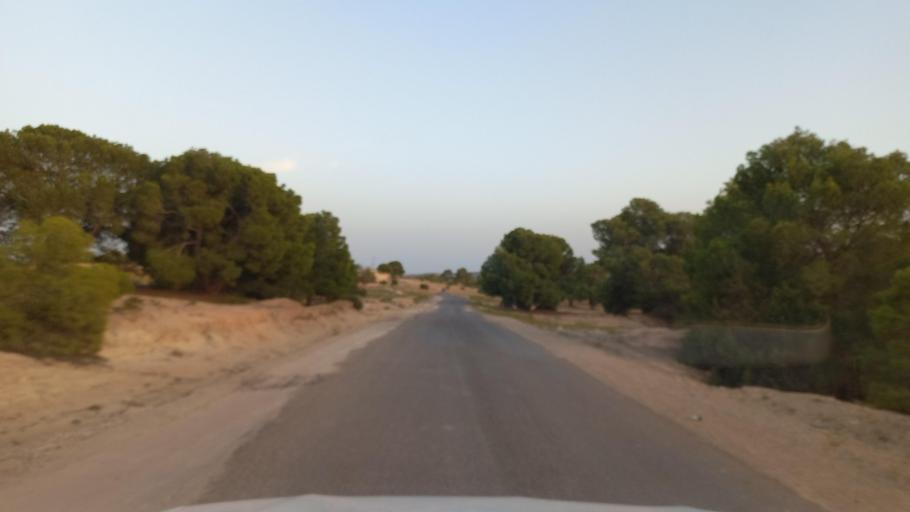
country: TN
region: Al Qasrayn
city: Sbiba
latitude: 35.4153
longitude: 8.9264
